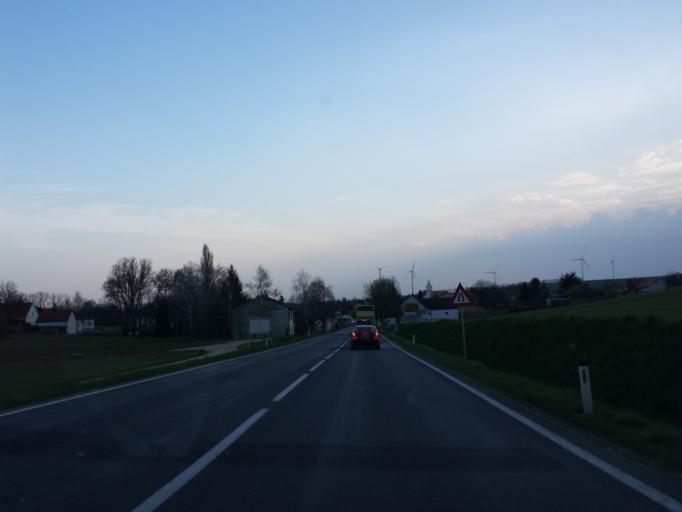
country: AT
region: Lower Austria
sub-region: Politischer Bezirk Mistelbach
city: Poysdorf
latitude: 48.6300
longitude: 16.6484
